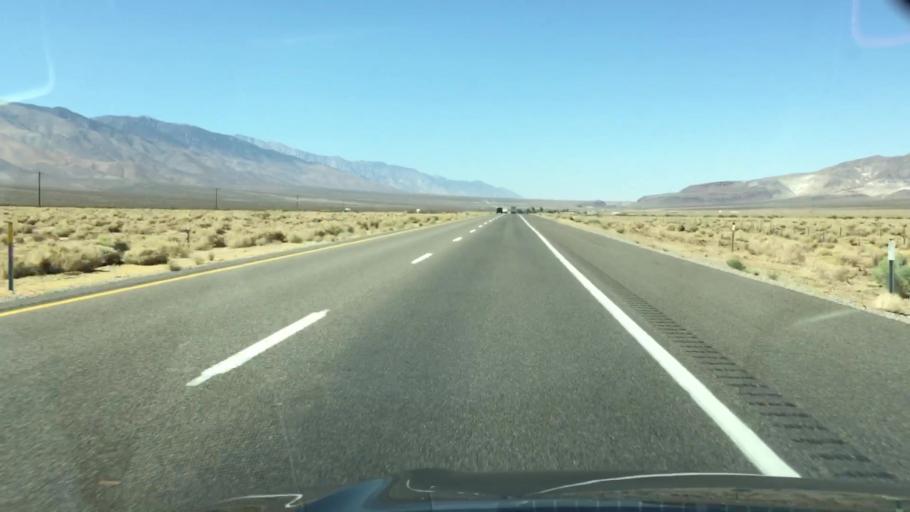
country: US
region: California
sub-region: Kern County
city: Inyokern
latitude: 36.0271
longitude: -117.9411
